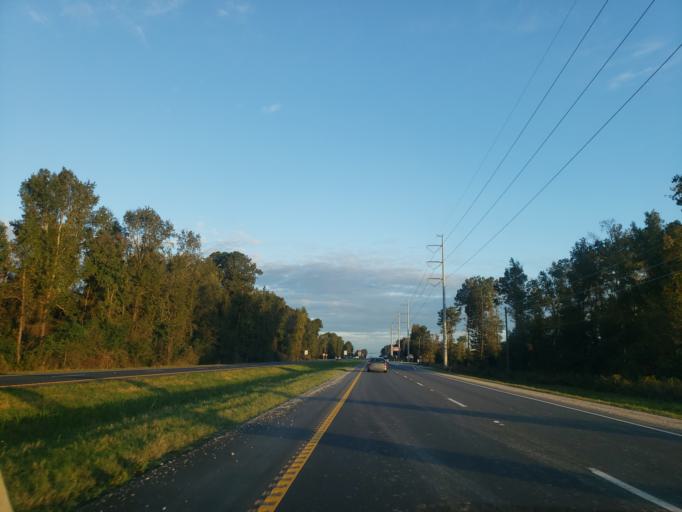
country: US
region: Georgia
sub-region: Chatham County
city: Port Wentworth
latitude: 32.1406
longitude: -81.1755
